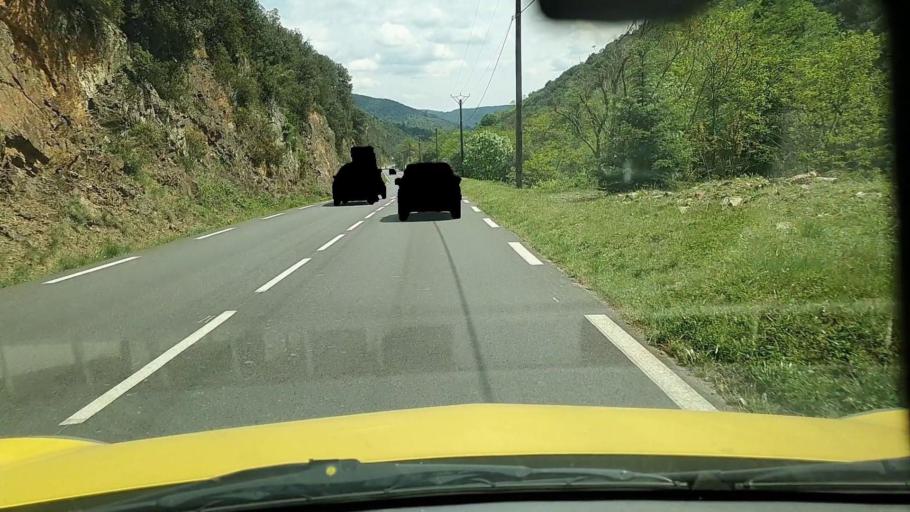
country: FR
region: Languedoc-Roussillon
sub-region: Departement du Gard
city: Valleraugue
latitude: 44.0752
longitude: 3.6690
